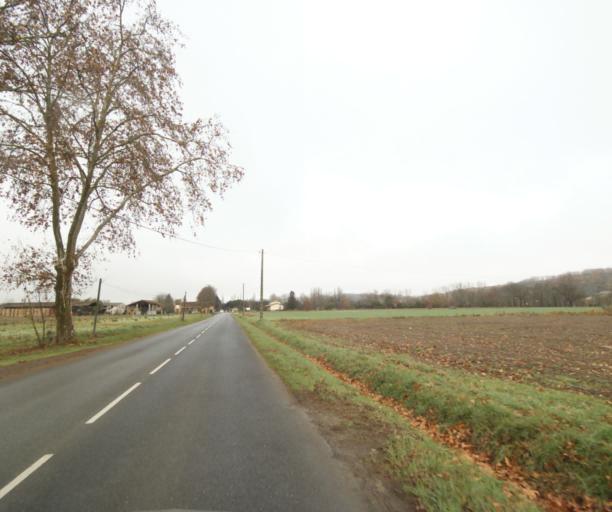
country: FR
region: Midi-Pyrenees
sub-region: Departement de la Haute-Garonne
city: Villemur-sur-Tarn
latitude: 43.8731
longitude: 1.4911
